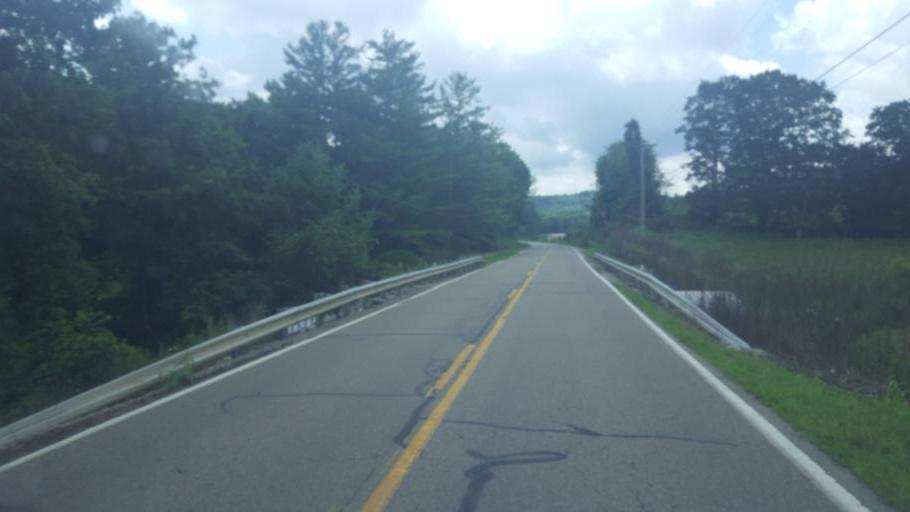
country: US
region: Ohio
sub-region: Ross County
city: Kingston
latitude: 39.4561
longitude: -82.7513
